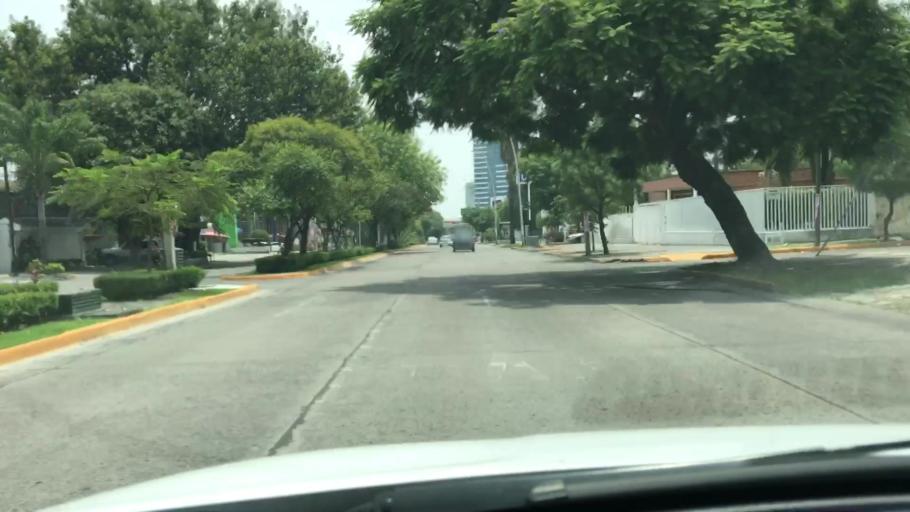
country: MX
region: Jalisco
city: Guadalajara
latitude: 20.6664
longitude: -103.3996
